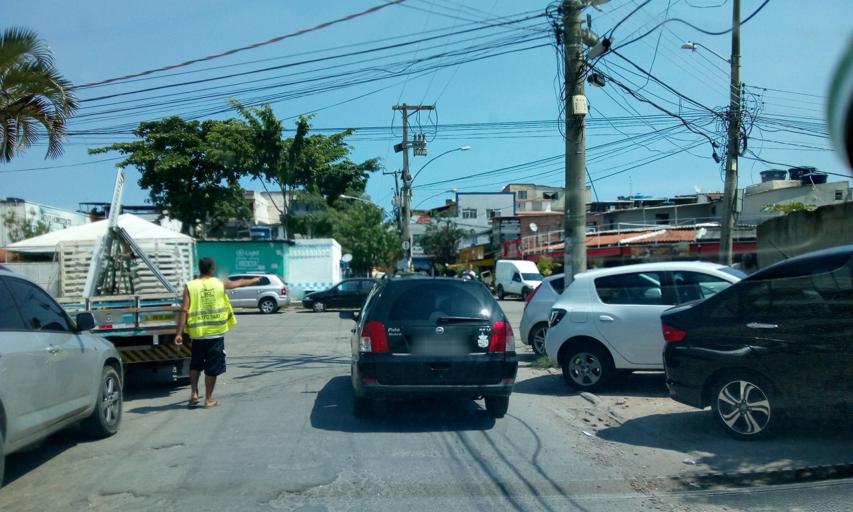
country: BR
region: Rio de Janeiro
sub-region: Nilopolis
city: Nilopolis
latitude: -23.0235
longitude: -43.4796
